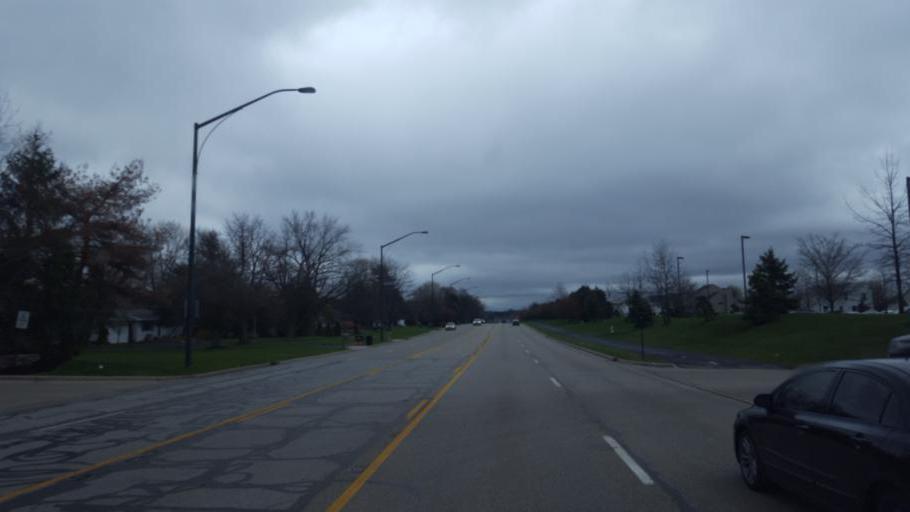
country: US
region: Ohio
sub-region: Franklin County
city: Westerville
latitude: 40.1384
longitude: -82.9640
